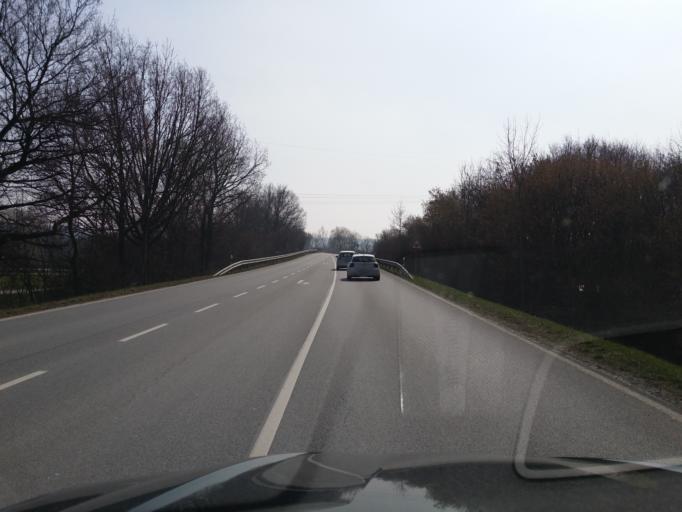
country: DE
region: Bavaria
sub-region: Lower Bavaria
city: Ergolding
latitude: 48.5671
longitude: 12.1775
